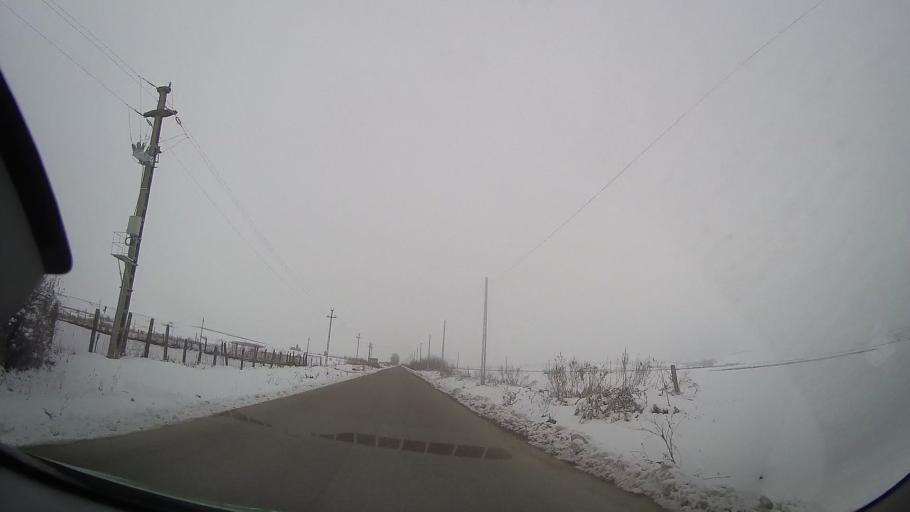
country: RO
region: Vaslui
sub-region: Comuna Todiresti
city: Todiresti
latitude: 46.8405
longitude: 27.3979
